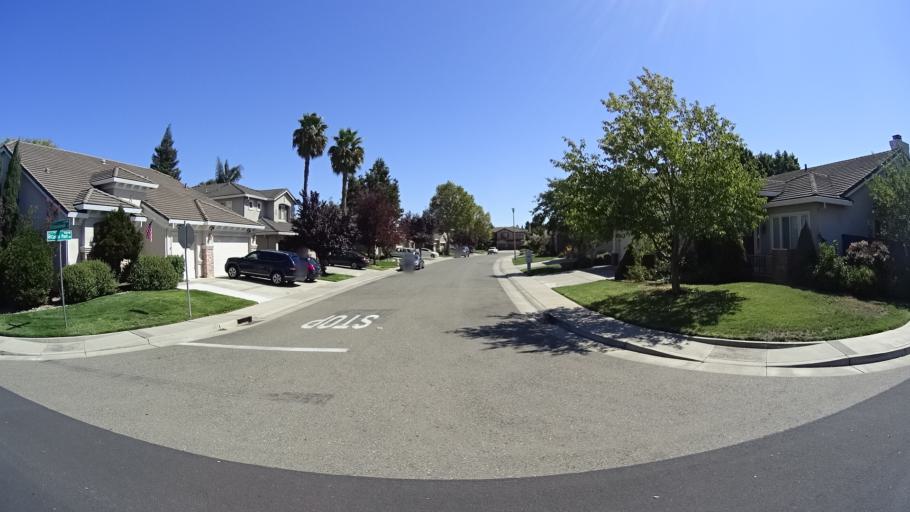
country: US
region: California
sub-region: Sacramento County
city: Elk Grove
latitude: 38.4123
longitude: -121.3463
